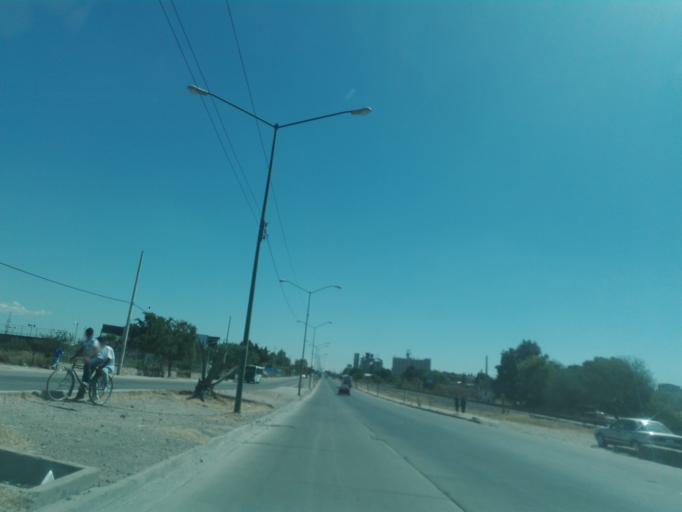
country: MX
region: Guanajuato
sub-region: Leon
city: San Jose de Duran (Los Troncoso)
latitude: 21.0888
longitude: -101.6740
